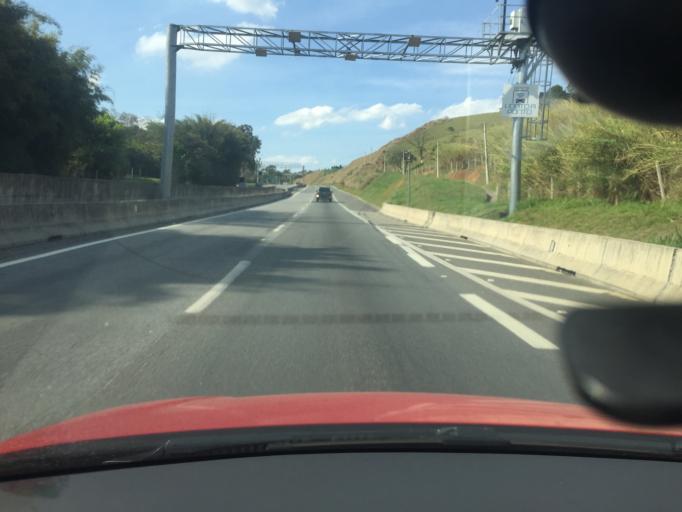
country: BR
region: Sao Paulo
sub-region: Jundiai
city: Jundiai
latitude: -23.1045
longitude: -46.8480
